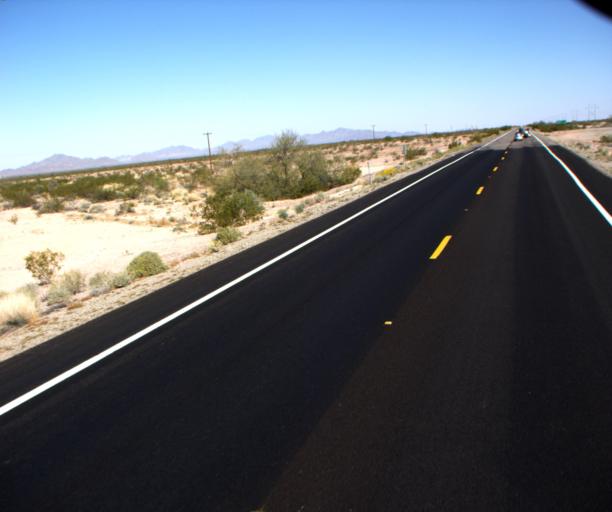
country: US
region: Arizona
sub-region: La Paz County
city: Quartzsite
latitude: 33.3106
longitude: -114.2169
